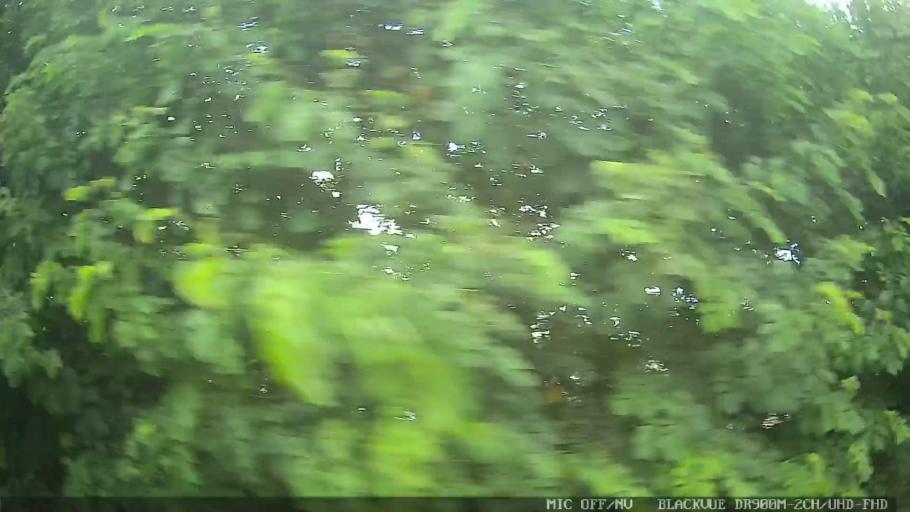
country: BR
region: Sao Paulo
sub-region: Braganca Paulista
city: Braganca Paulista
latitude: -22.9900
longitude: -46.4850
